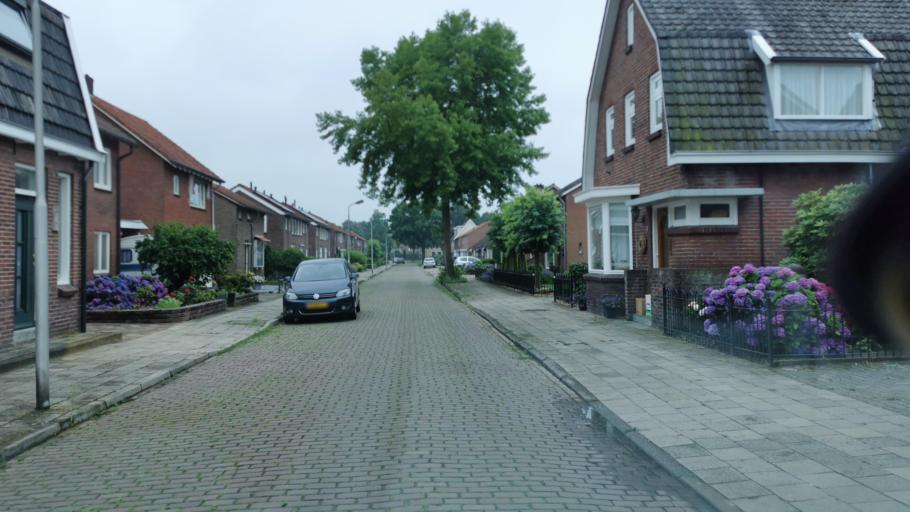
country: NL
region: Overijssel
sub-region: Gemeente Losser
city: Losser
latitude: 52.2604
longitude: 7.0101
